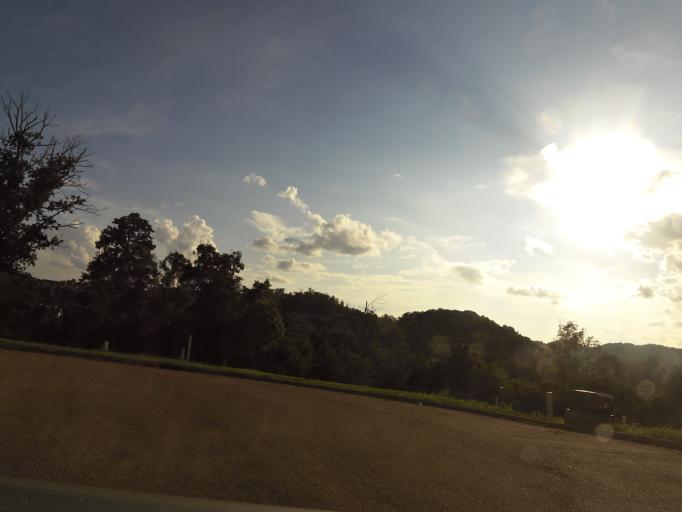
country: US
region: Tennessee
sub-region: Knox County
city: Knoxville
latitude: 36.0006
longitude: -84.0188
